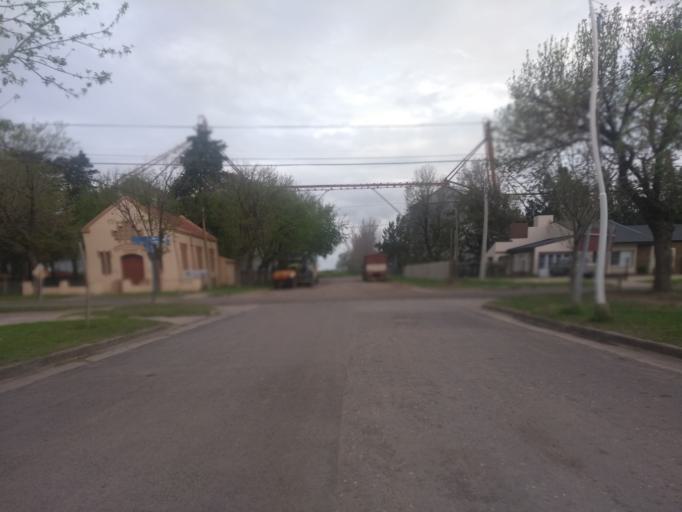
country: AR
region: Santa Fe
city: Galvez
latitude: -31.9066
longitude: -61.2786
